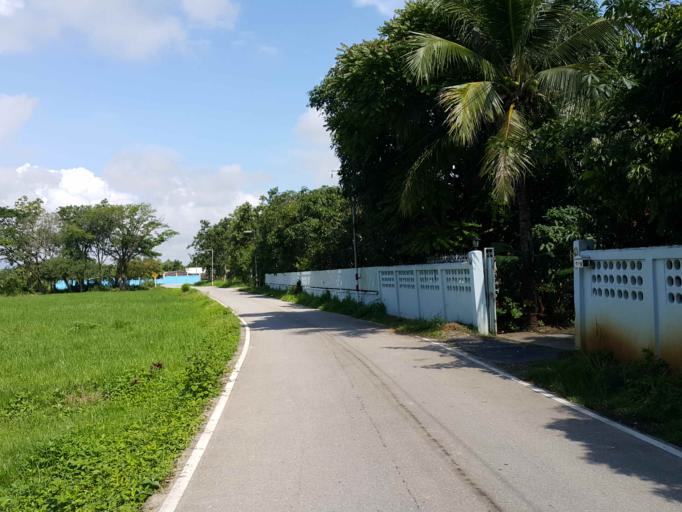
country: TH
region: Chiang Mai
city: San Kamphaeng
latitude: 18.8100
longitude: 99.1033
